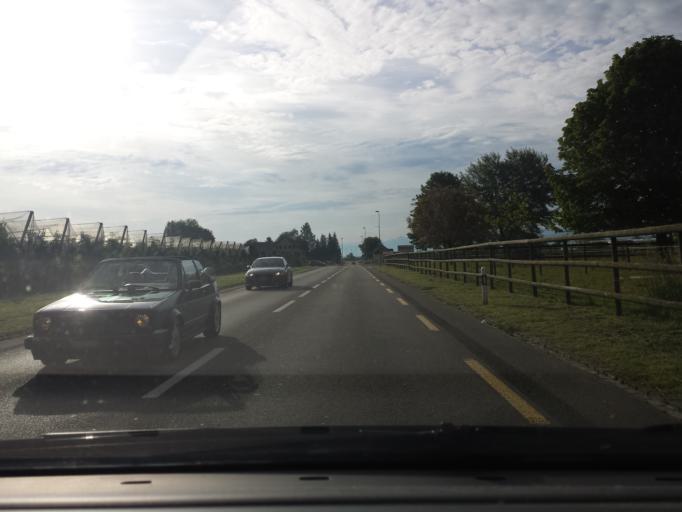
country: CH
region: Thurgau
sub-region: Arbon District
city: Egnach
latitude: 47.5258
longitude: 9.3842
